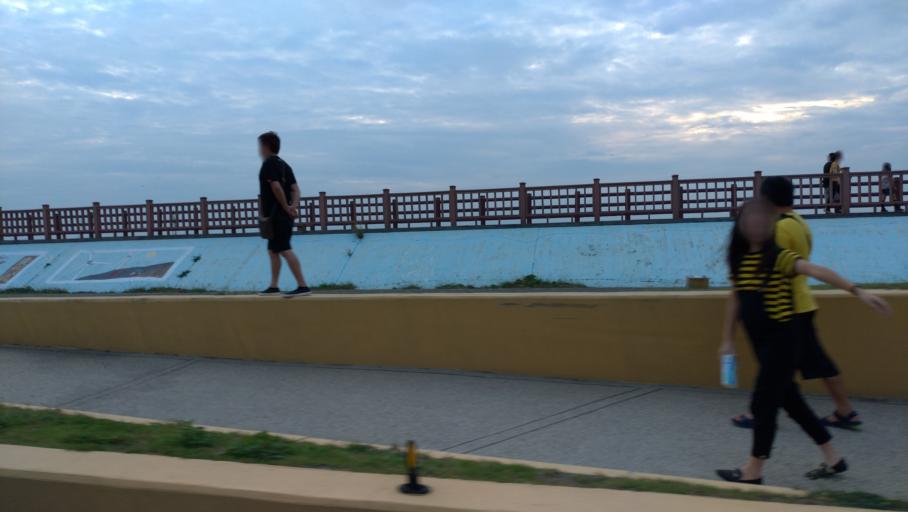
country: TW
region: Taiwan
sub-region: Hsinchu
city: Hsinchu
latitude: 24.7798
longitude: 120.9147
